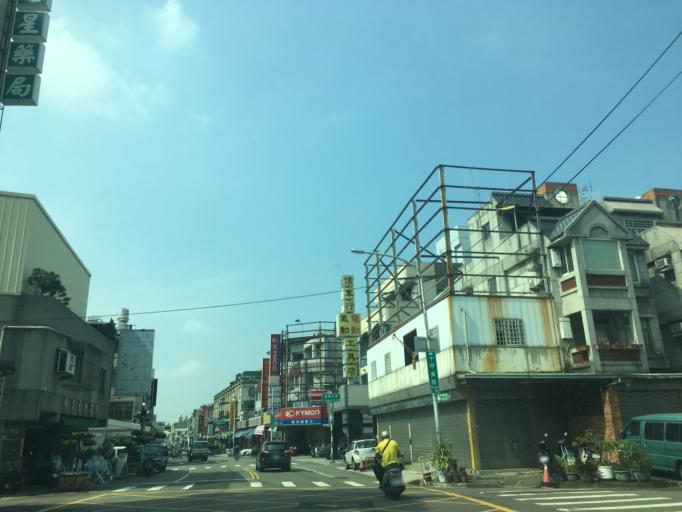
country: TW
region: Taiwan
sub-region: Taichung City
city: Taichung
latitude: 24.1363
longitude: 120.7061
